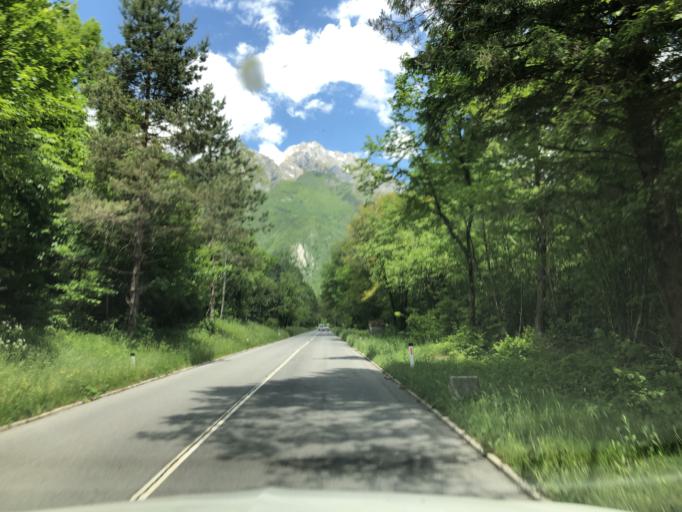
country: SI
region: Bovec
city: Bovec
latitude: 46.3508
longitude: 13.5809
